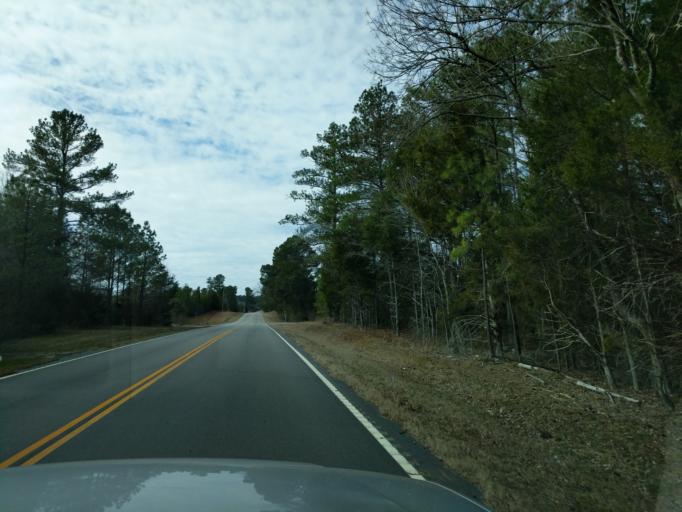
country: US
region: South Carolina
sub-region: Edgefield County
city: Edgefield
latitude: 33.9296
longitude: -81.9965
